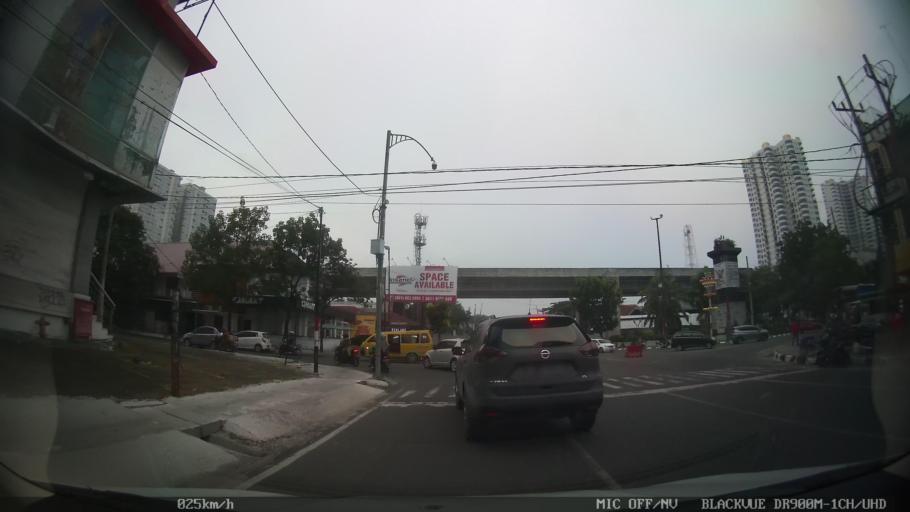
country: ID
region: North Sumatra
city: Medan
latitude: 3.5934
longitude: 98.6778
